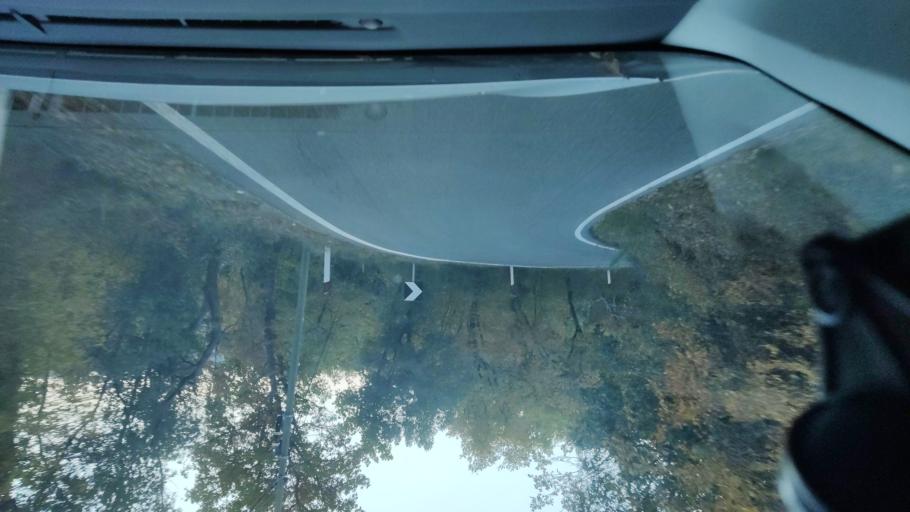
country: IT
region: Umbria
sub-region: Provincia di Terni
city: Amelia
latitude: 42.5889
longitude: 12.4342
